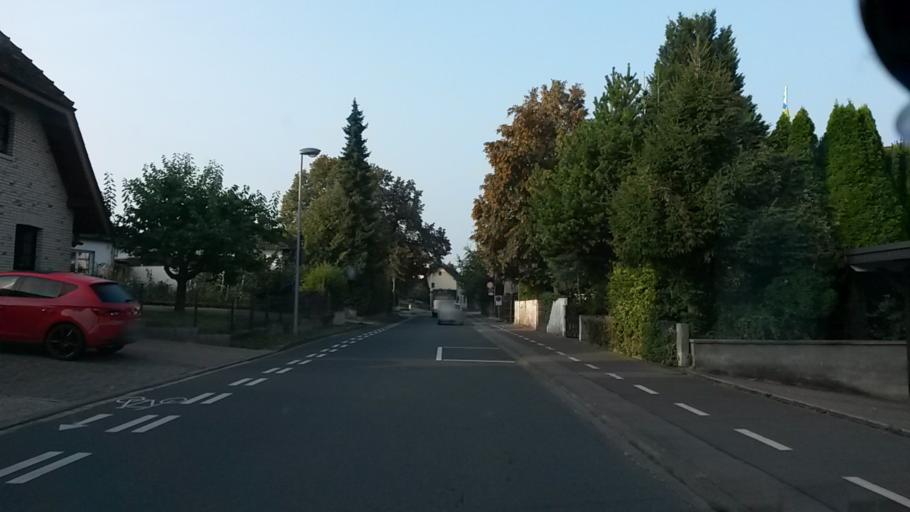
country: DE
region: North Rhine-Westphalia
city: Lohmar
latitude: 50.8379
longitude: 7.2111
